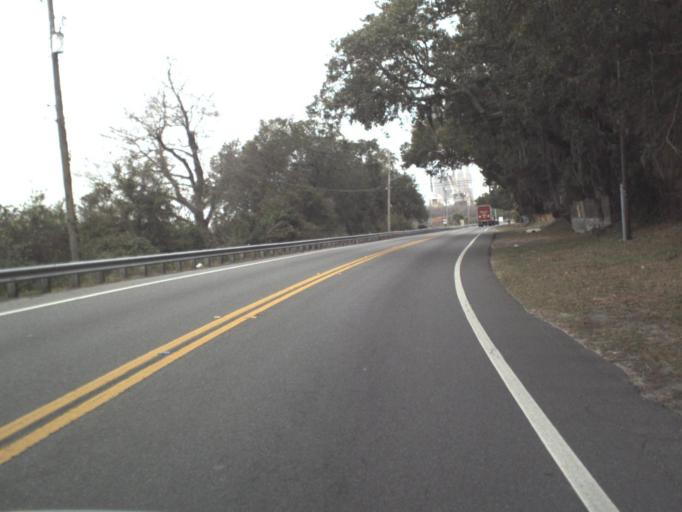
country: US
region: Florida
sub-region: Bay County
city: Parker
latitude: 30.1321
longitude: -85.6136
